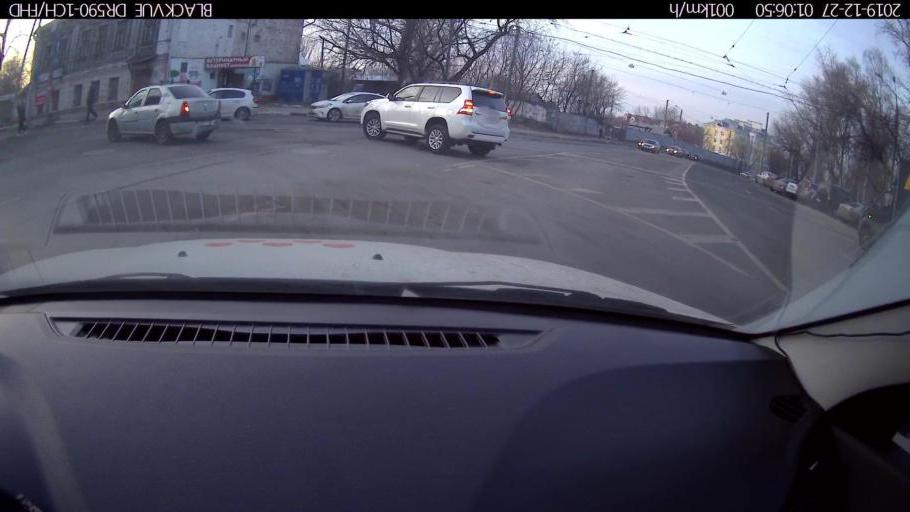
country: RU
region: Nizjnij Novgorod
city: Nizhniy Novgorod
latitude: 56.3161
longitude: 43.9844
